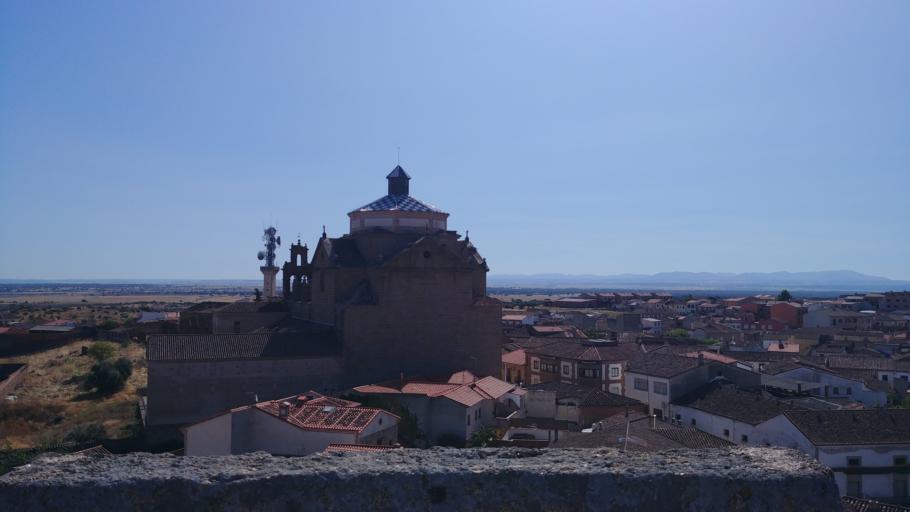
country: ES
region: Castille-La Mancha
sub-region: Province of Toledo
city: Oropesa
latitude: 39.9198
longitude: -5.1738
